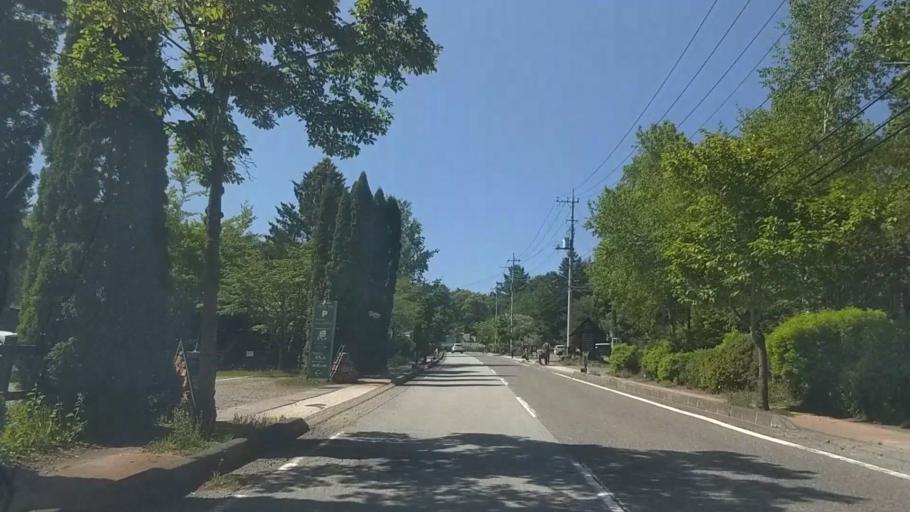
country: JP
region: Yamanashi
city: Nirasaki
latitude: 35.8959
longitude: 138.4381
